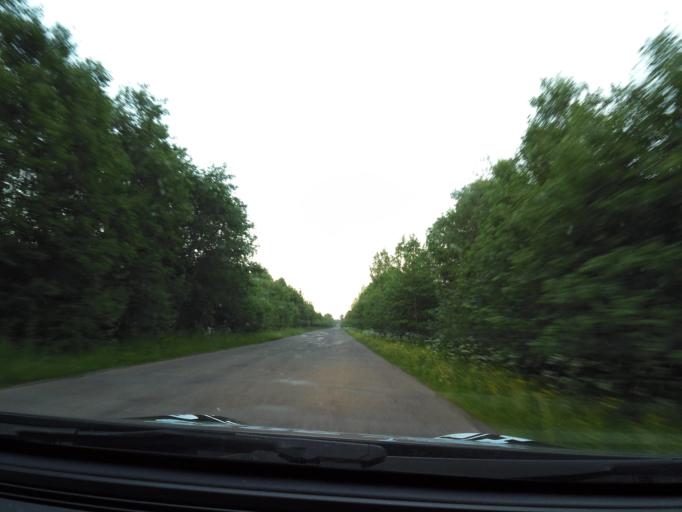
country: RU
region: Leningrad
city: Voznesen'ye
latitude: 60.8273
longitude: 35.7132
